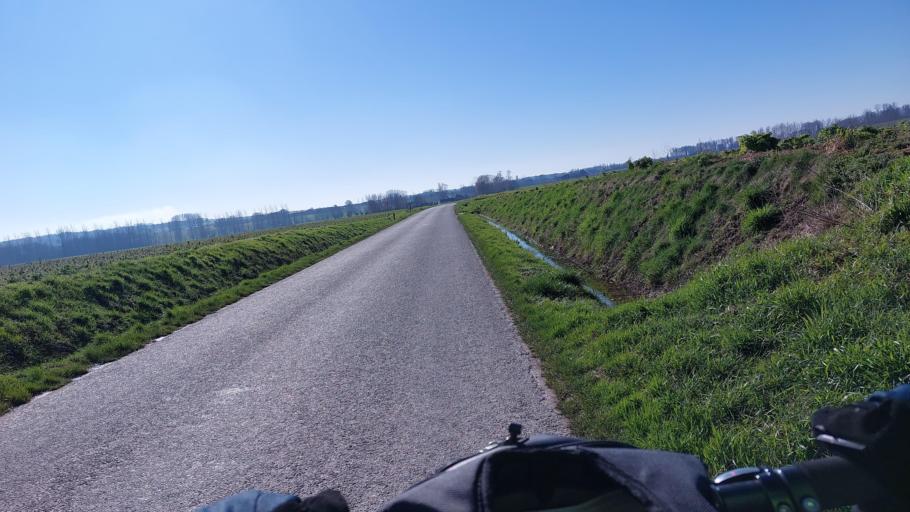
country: BE
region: Wallonia
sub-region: Province du Hainaut
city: Silly
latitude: 50.6217
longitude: 3.8925
